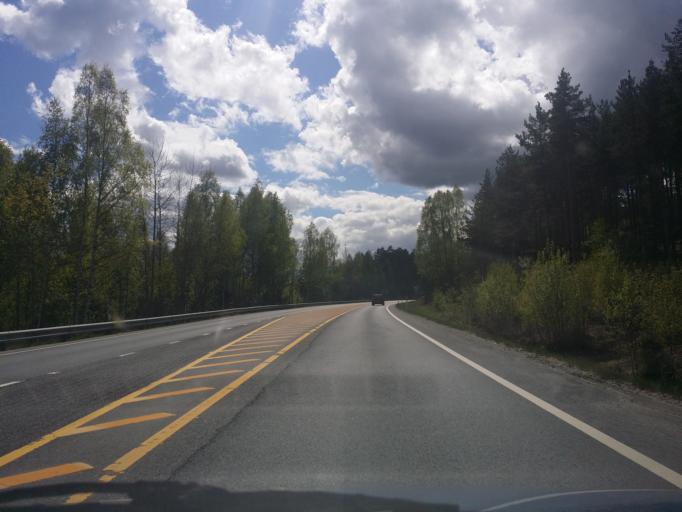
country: NO
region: Buskerud
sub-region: Modum
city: Vikersund
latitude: 59.9437
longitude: 9.9667
